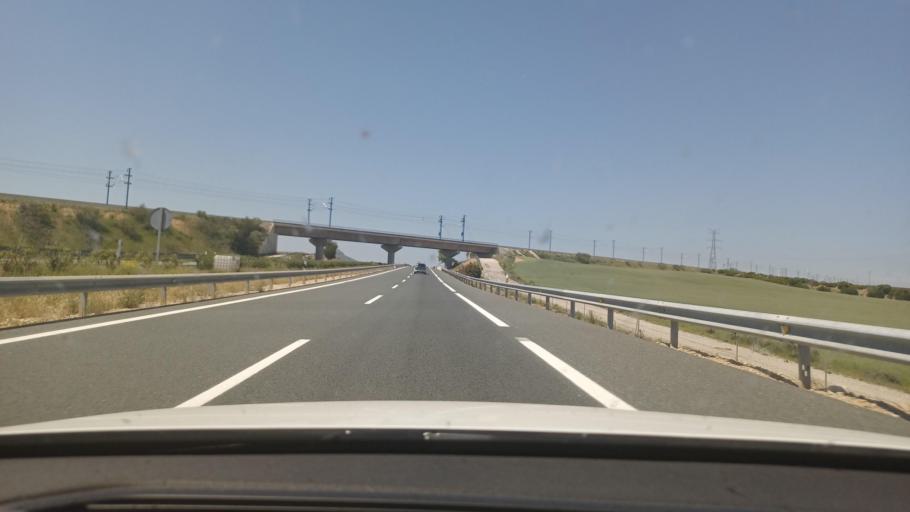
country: ES
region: Castille-La Mancha
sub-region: Provincia de Albacete
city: Alpera
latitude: 38.8803
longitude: -1.2533
